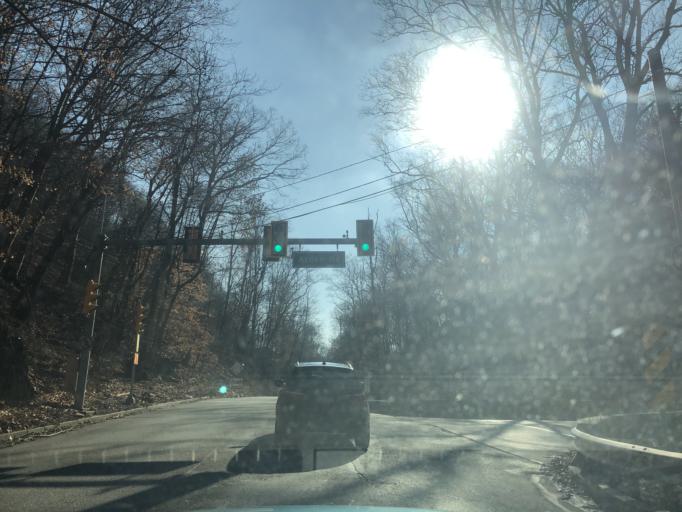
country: US
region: Pennsylvania
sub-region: Delaware County
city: Radnor
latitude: 40.0661
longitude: -75.3429
